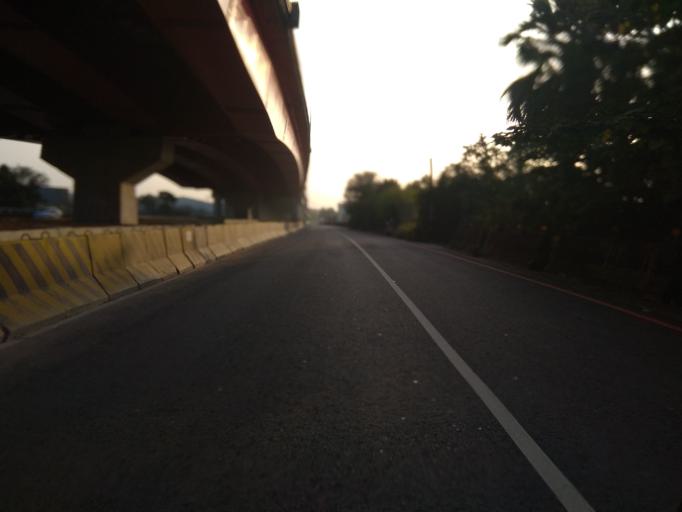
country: TW
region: Taiwan
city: Daxi
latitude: 24.9283
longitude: 121.2073
